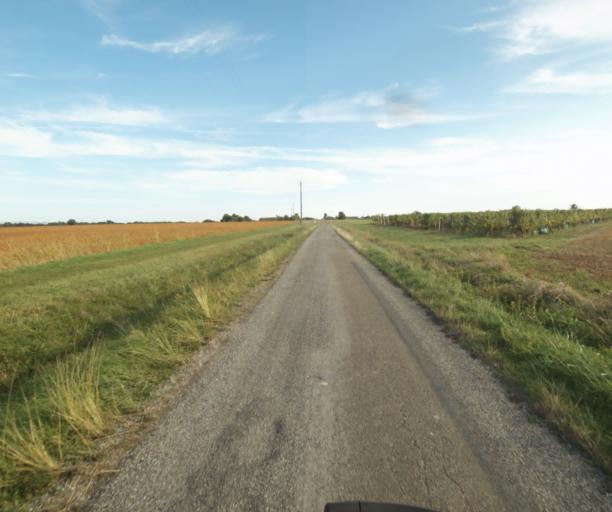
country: FR
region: Midi-Pyrenees
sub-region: Departement du Tarn-et-Garonne
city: Finhan
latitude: 43.9067
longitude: 1.1295
